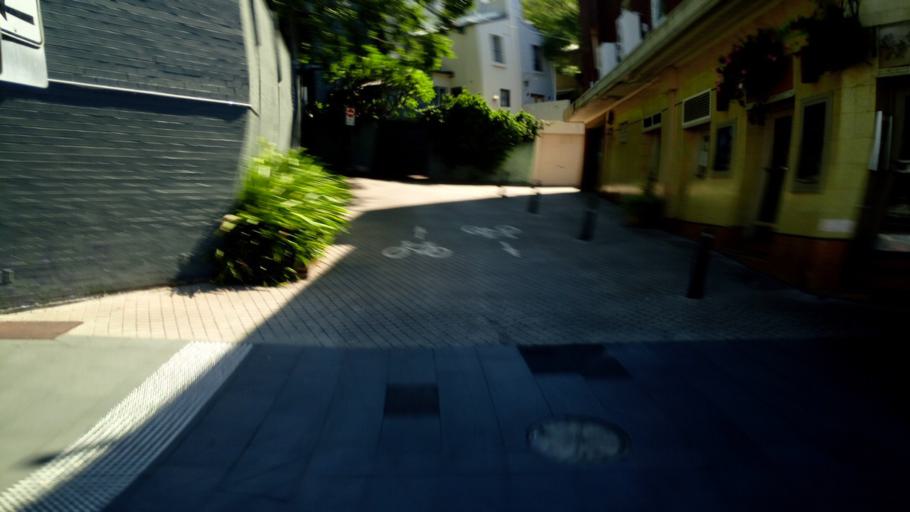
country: AU
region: New South Wales
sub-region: City of Sydney
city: Darlinghurst
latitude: -33.8832
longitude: 151.2207
